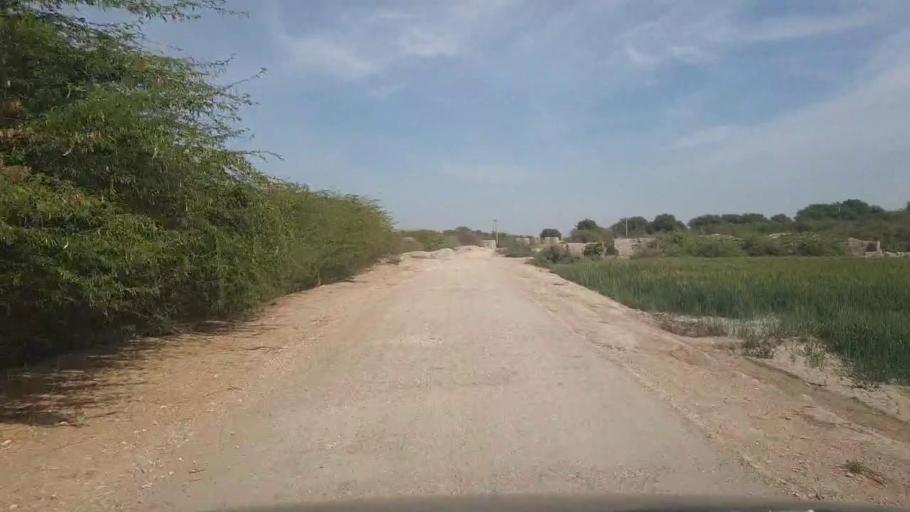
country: PK
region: Sindh
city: Kunri
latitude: 25.2244
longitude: 69.6558
